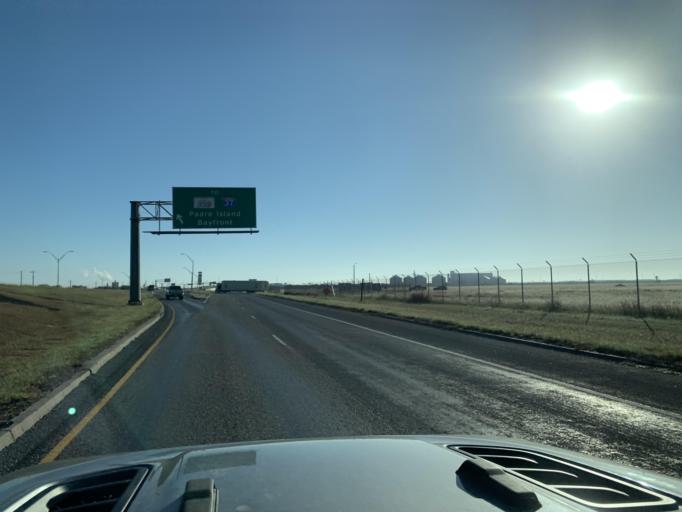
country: US
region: Texas
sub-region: Nueces County
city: Corpus Christi
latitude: 27.7846
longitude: -97.5000
